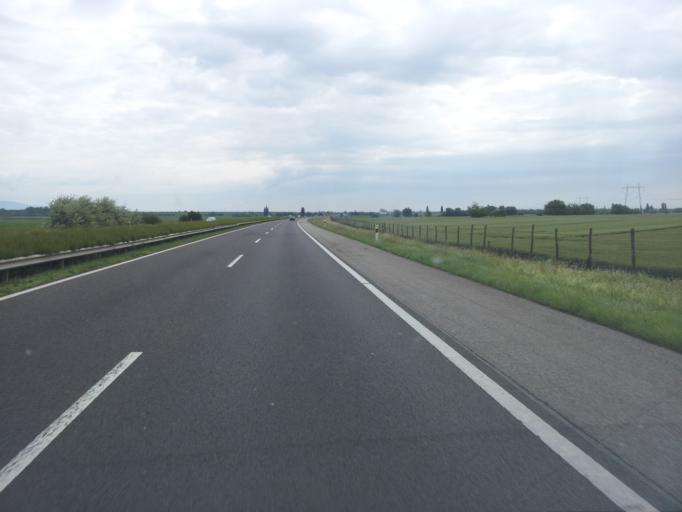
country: HU
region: Heves
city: Hort
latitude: 47.7035
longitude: 19.7869
